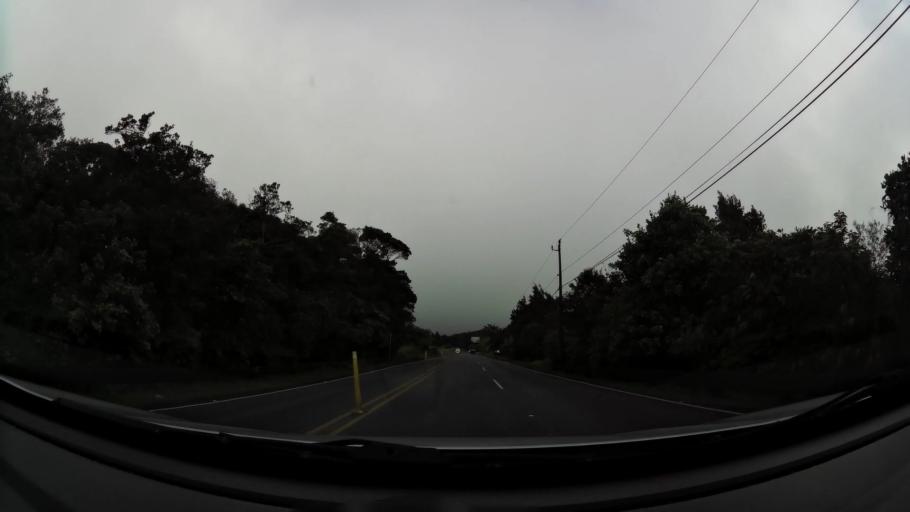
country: CR
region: Heredia
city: Angeles
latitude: 10.0340
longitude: -84.0030
